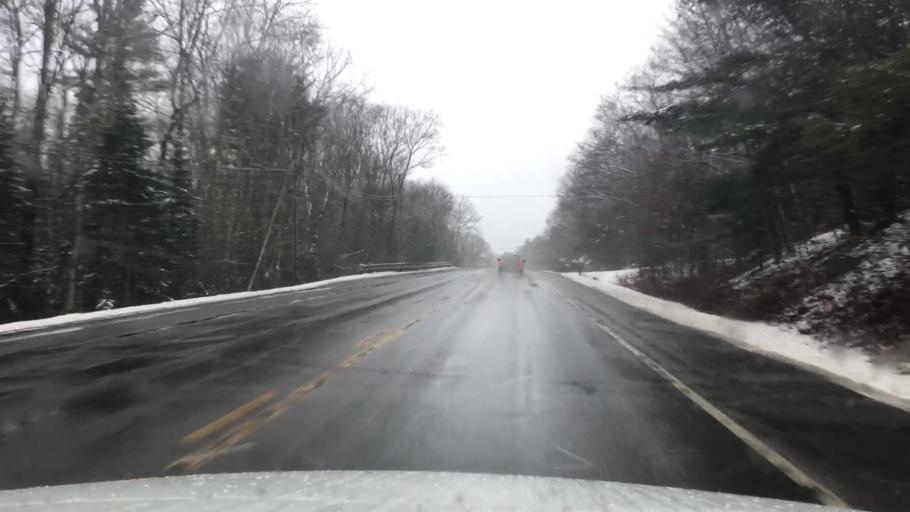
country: US
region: Maine
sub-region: Knox County
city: Warren
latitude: 44.1390
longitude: -69.2158
